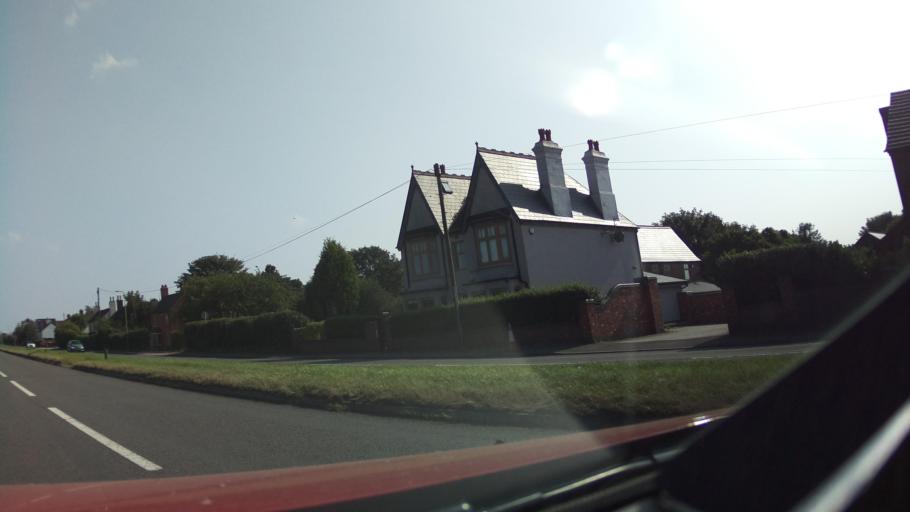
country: GB
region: England
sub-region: Staffordshire
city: Chasetown
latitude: 52.6534
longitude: -1.8867
